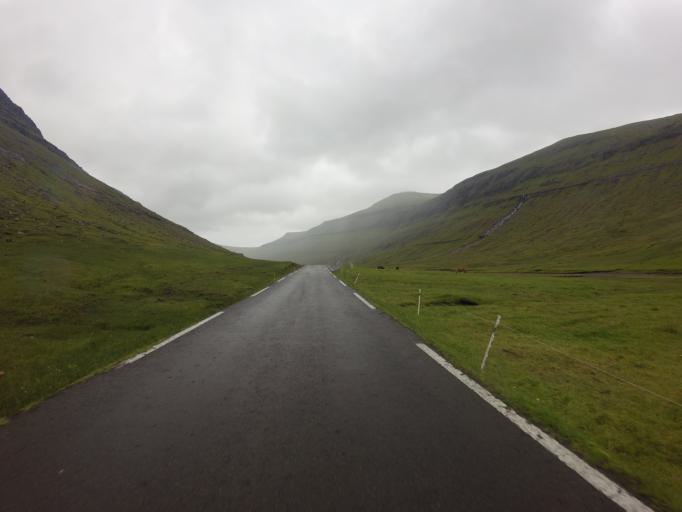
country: FO
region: Streymoy
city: Vestmanna
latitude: 62.2312
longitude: -7.1378
